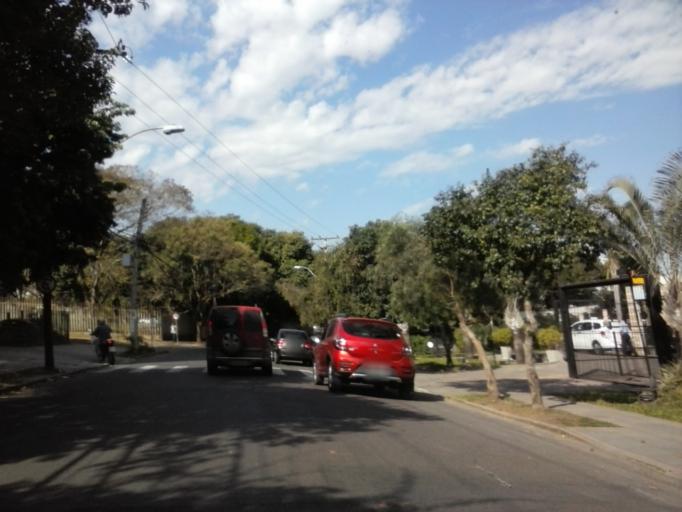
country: BR
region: Rio Grande do Sul
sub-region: Porto Alegre
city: Porto Alegre
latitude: -30.0505
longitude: -51.1851
